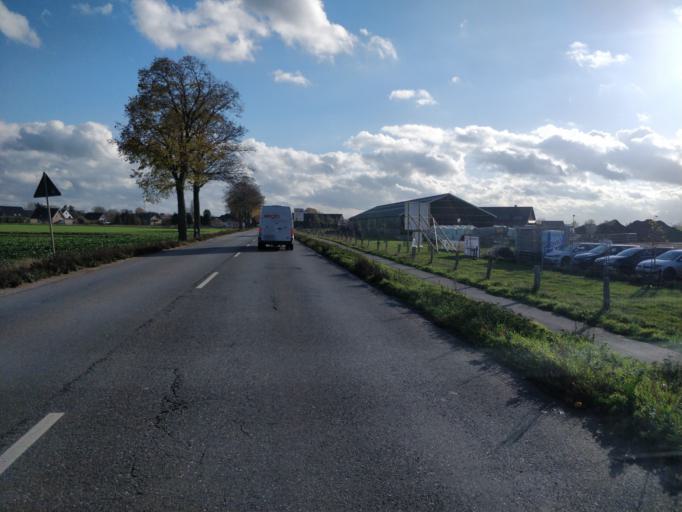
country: DE
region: North Rhine-Westphalia
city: Rees
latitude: 51.8069
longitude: 6.3664
